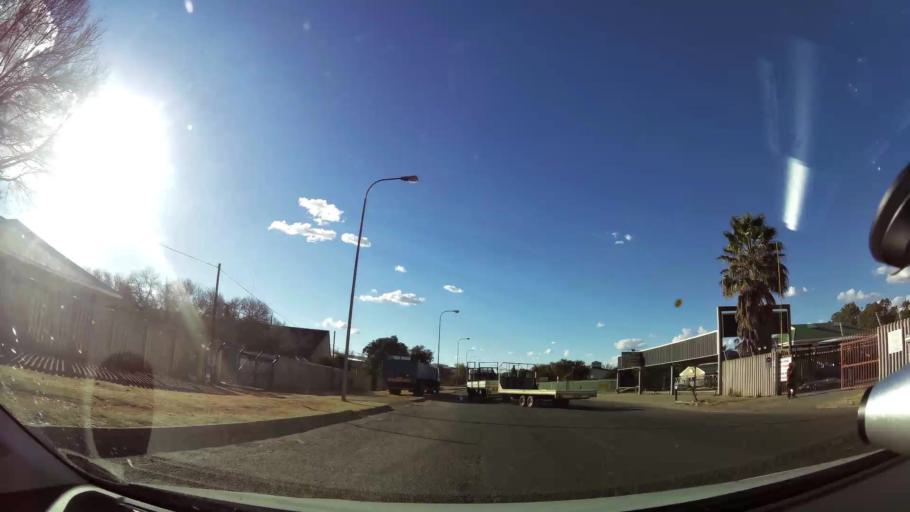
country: ZA
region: North-West
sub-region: Dr Kenneth Kaunda District Municipality
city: Klerksdorp
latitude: -26.8627
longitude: 26.6690
